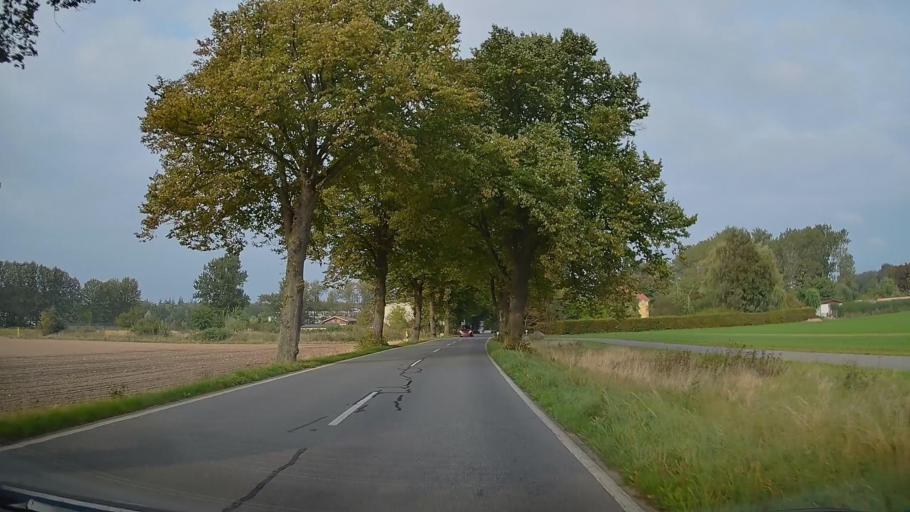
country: DE
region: Mecklenburg-Vorpommern
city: Bad Doberan
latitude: 54.1360
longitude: 11.8364
